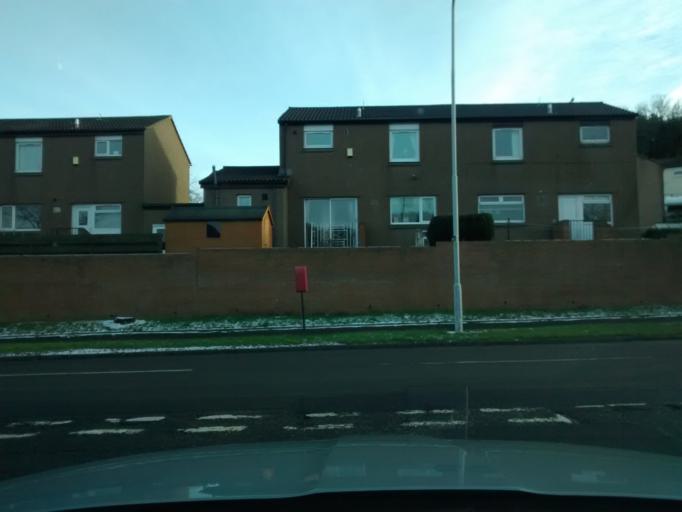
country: GB
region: Scotland
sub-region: Fife
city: Inverkeithing
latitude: 56.0332
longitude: -3.3637
